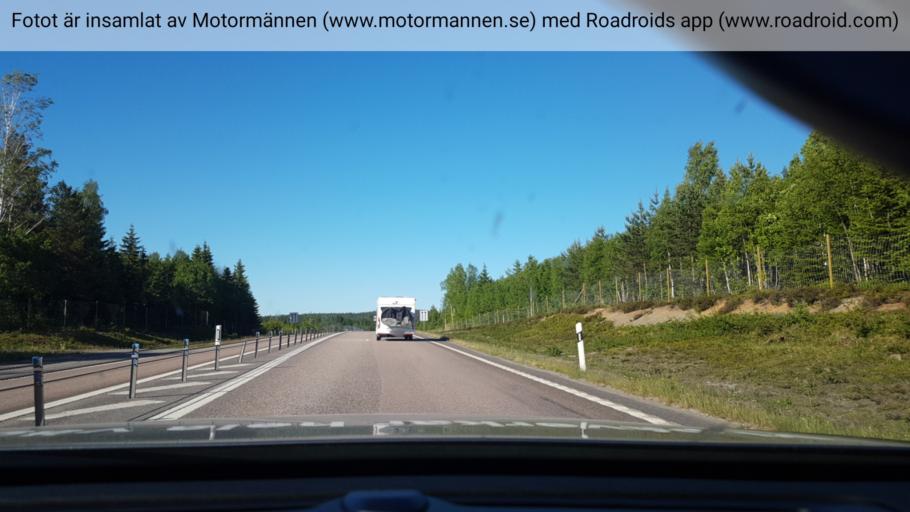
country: SE
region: Vaesternorrland
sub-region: Haernoesands Kommun
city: Haernoesand
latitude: 62.6017
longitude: 17.8138
